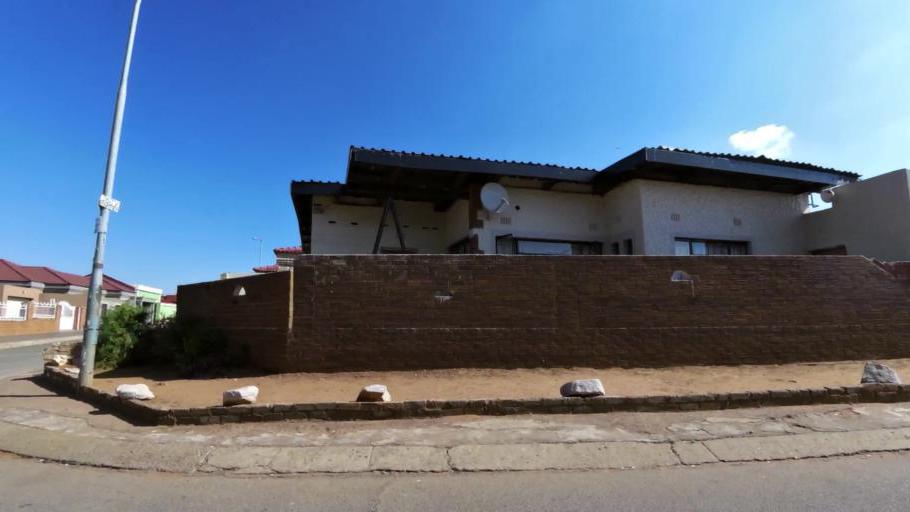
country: ZA
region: Gauteng
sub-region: City of Johannesburg Metropolitan Municipality
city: Soweto
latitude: -26.2350
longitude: 27.8862
